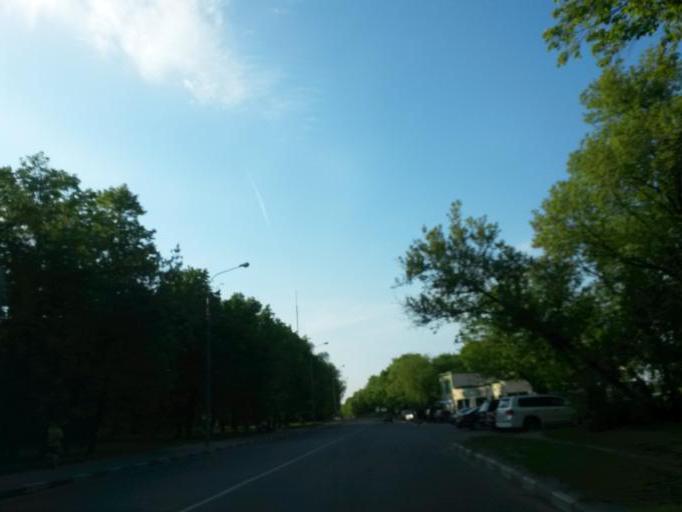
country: RU
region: Moscow
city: Zagor'ye
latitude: 55.5832
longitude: 37.6586
